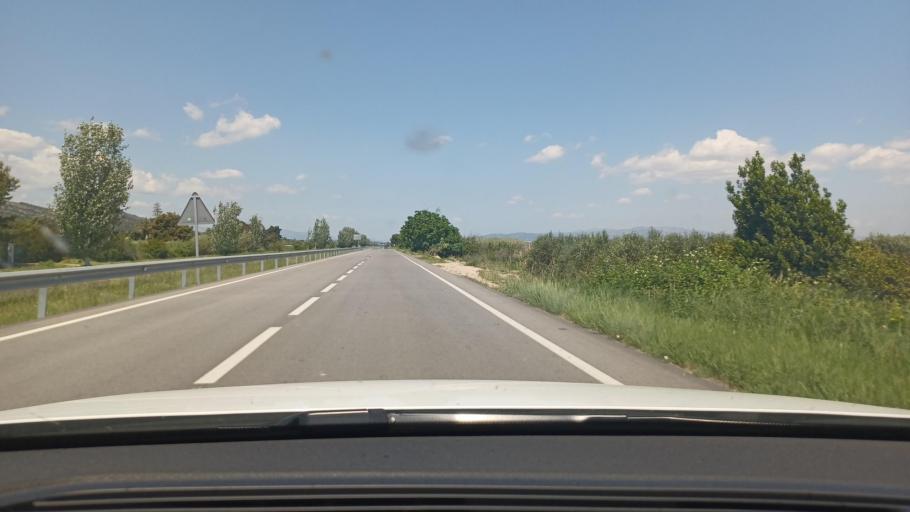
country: ES
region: Catalonia
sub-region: Provincia de Tarragona
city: Sant Carles de la Rapita
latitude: 40.6449
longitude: 0.5994
